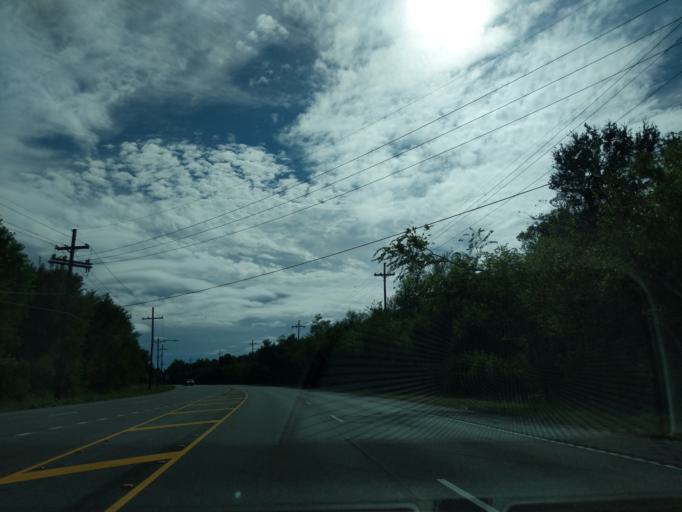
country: US
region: Louisiana
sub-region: Saint Bernard Parish
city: Meraux
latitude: 30.0739
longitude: -89.8625
